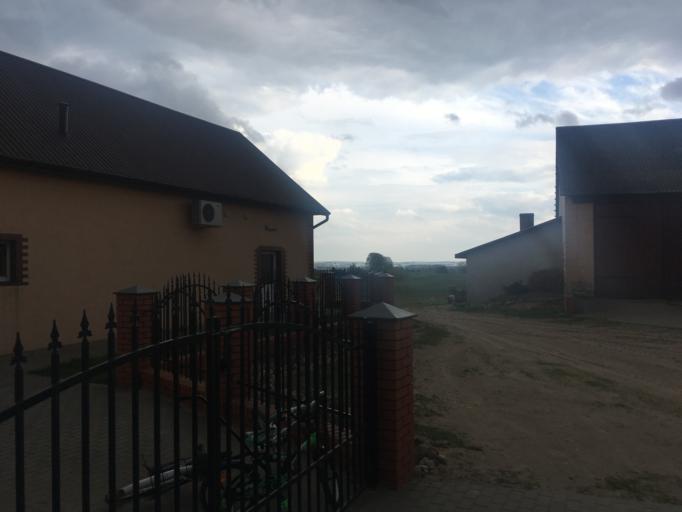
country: PL
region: Podlasie
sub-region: Powiat sejnenski
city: Punsk
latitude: 54.3839
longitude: 22.9707
